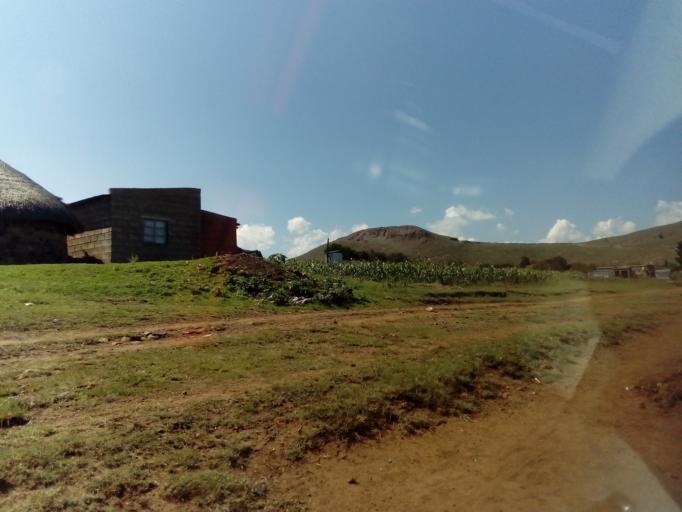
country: LS
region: Berea
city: Teyateyaneng
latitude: -29.2258
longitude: 27.8685
